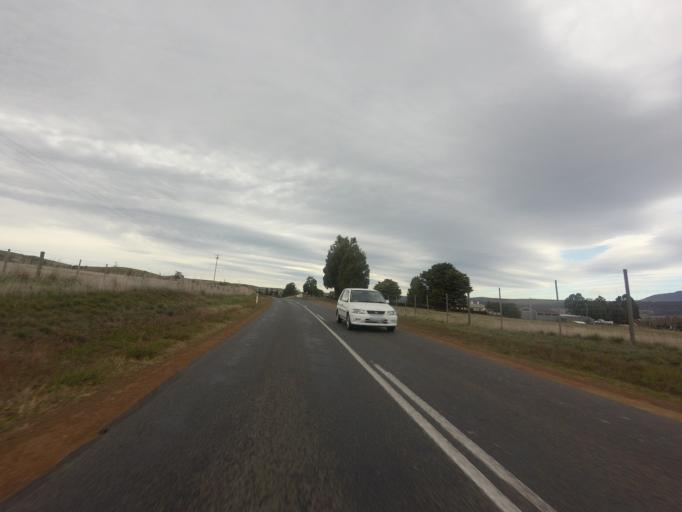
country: AU
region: Tasmania
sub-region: Derwent Valley
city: New Norfolk
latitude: -42.5131
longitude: 146.7432
